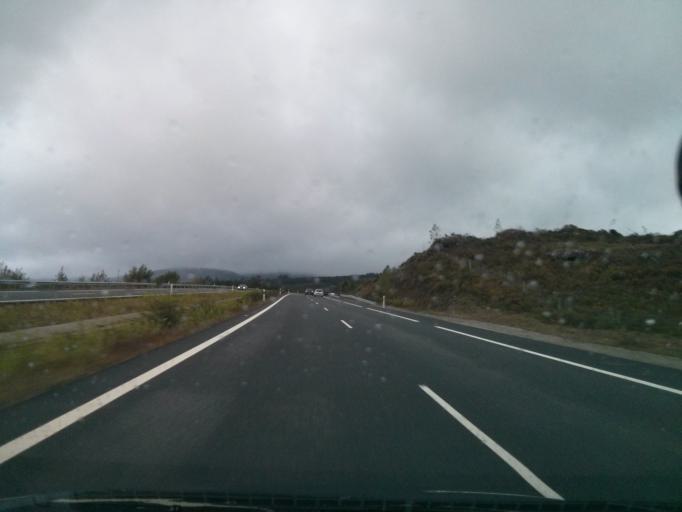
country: ES
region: Galicia
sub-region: Provincia de Pontevedra
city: Covelo
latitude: 42.1999
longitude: -8.2960
